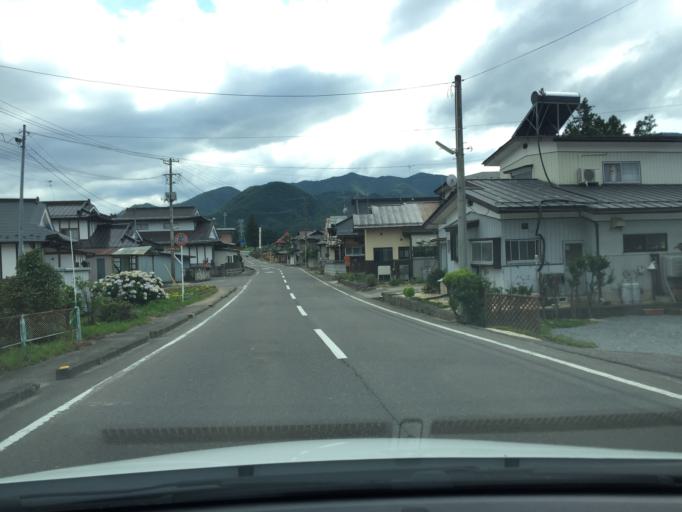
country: JP
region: Fukushima
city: Sukagawa
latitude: 37.2778
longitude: 140.1665
